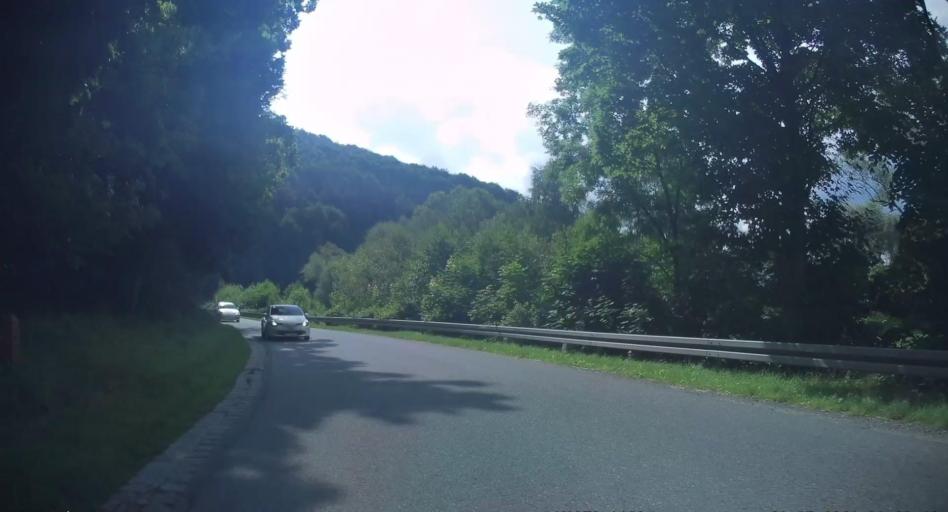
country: PL
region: Lower Silesian Voivodeship
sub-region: Powiat walbrzyski
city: Walim
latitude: 50.7432
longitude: 16.4088
